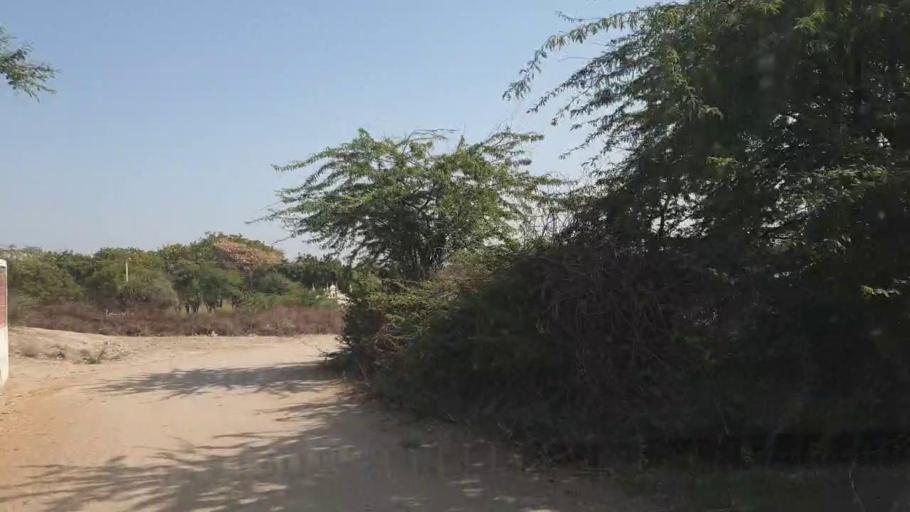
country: PK
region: Sindh
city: Dhoro Naro
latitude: 25.4960
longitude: 69.6279
